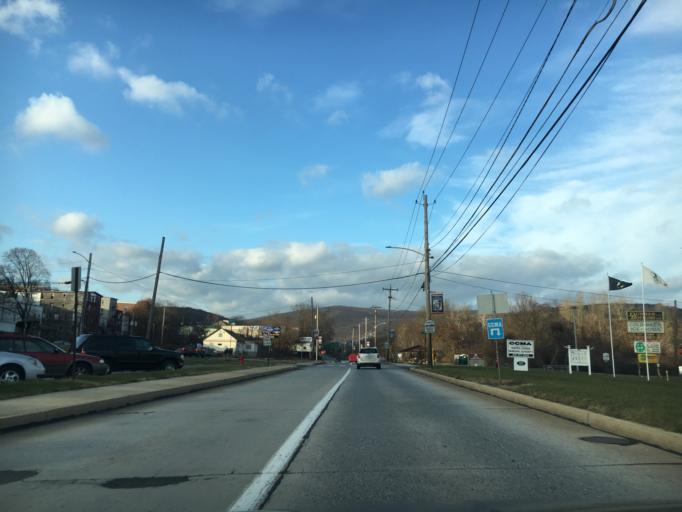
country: US
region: Pennsylvania
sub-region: Carbon County
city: Lehighton
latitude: 40.8339
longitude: -75.7073
